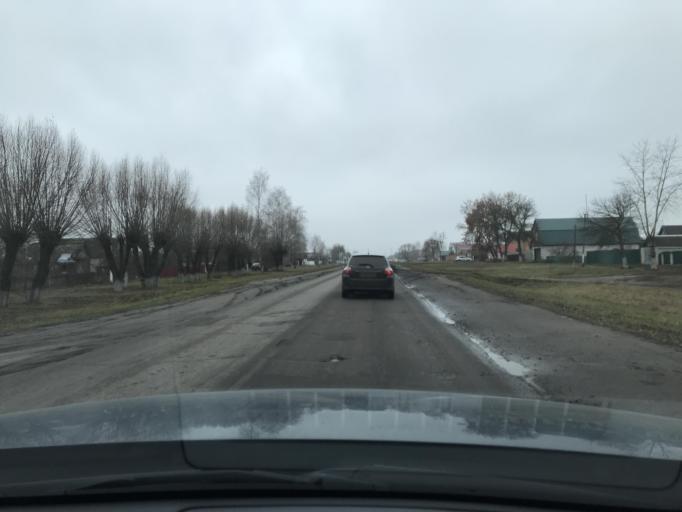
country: RU
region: Penza
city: Zemetchino
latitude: 53.4998
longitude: 42.6289
